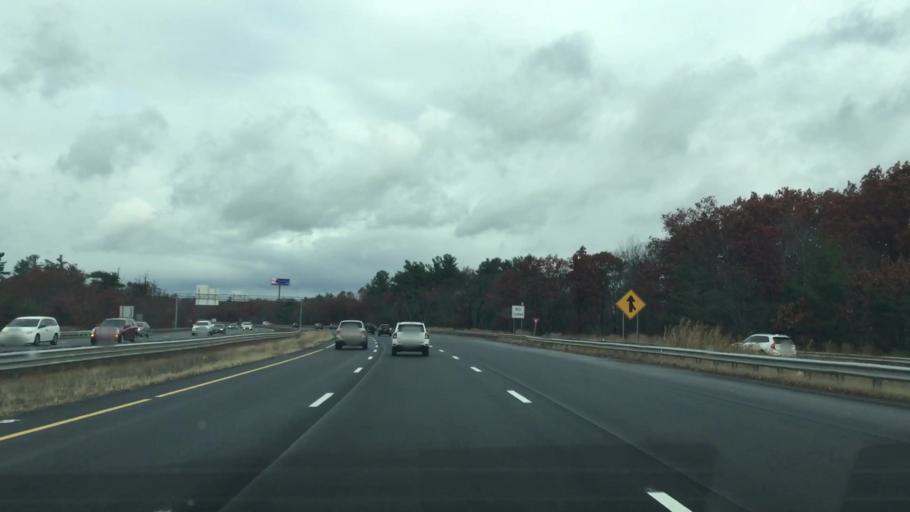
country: US
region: Massachusetts
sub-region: Essex County
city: Methuen
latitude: 42.7365
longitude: -71.2039
